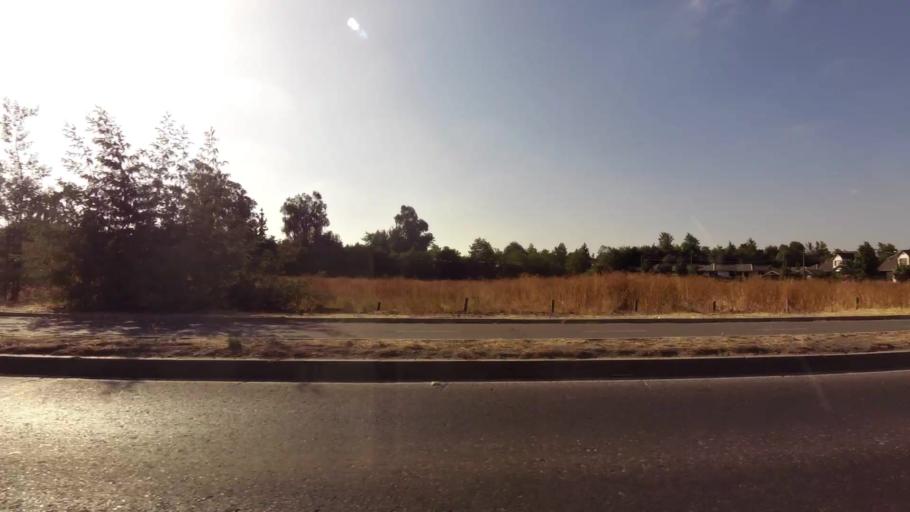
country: CL
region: Maule
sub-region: Provincia de Talca
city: Talca
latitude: -35.4137
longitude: -71.6719
